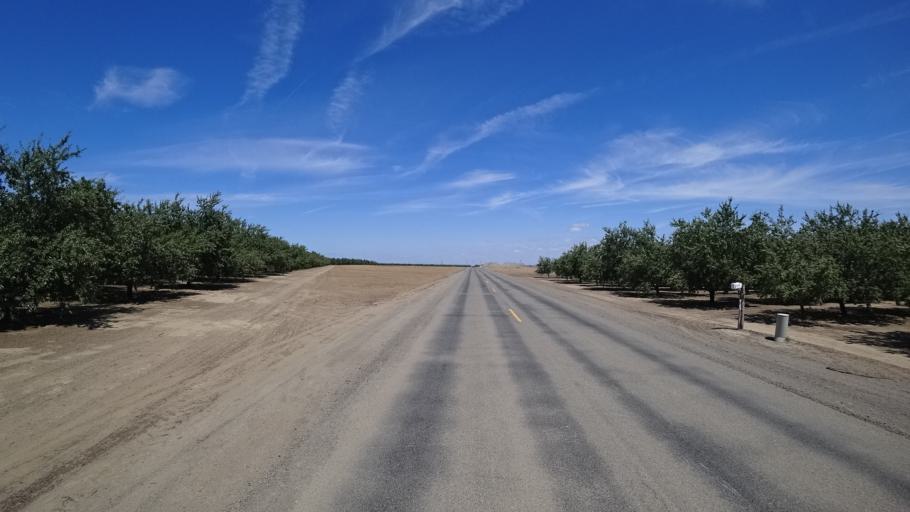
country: US
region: California
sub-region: Kings County
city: Kettleman City
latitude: 35.9303
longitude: -119.9149
